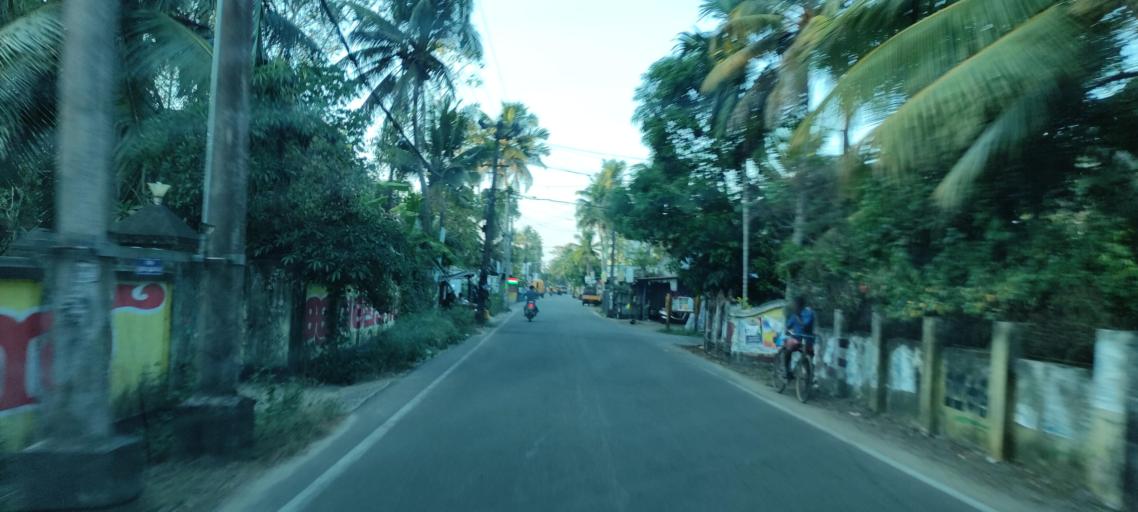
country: IN
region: Kerala
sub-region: Alappuzha
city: Kayankulam
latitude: 9.2234
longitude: 76.4598
